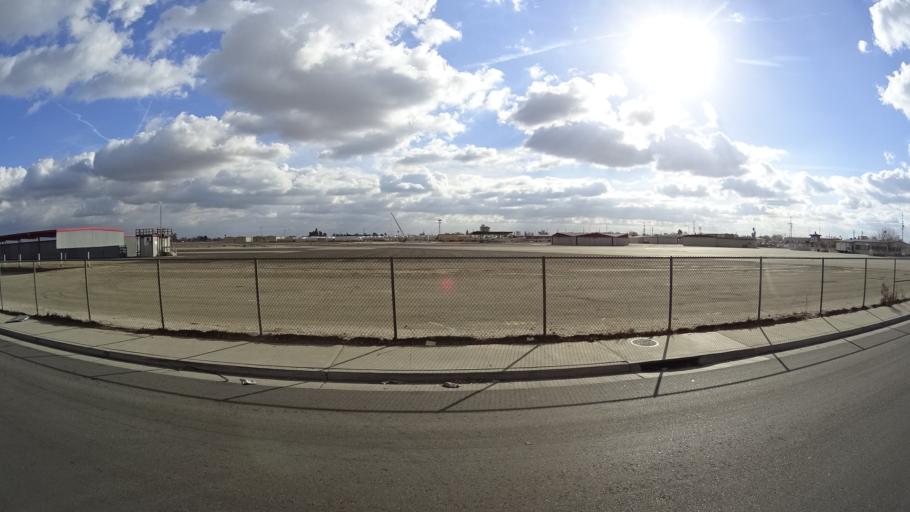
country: US
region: California
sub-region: Kern County
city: Bakersfield
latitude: 35.3322
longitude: -119.0005
